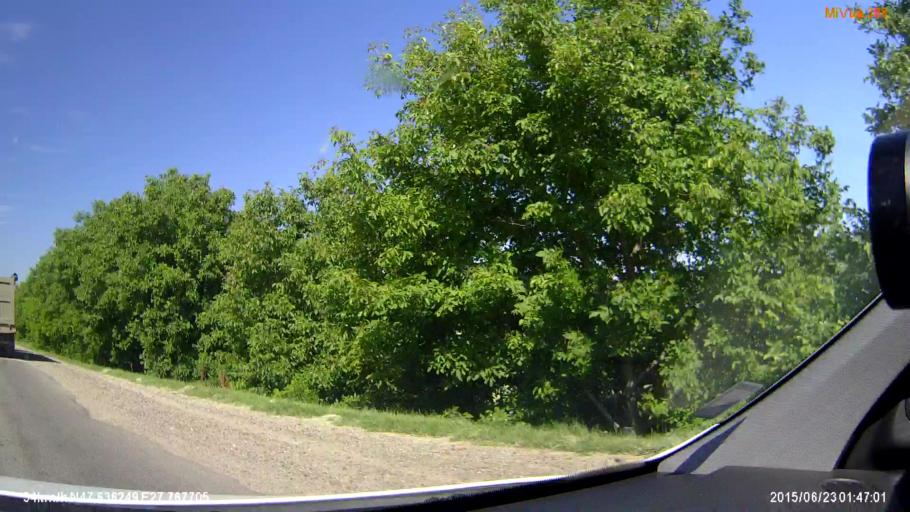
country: MD
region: Falesti
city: Falesti
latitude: 47.6361
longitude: 27.7676
